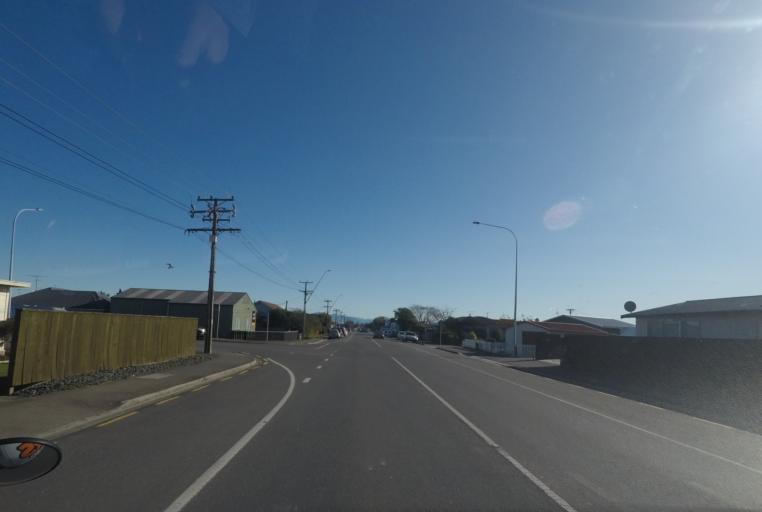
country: NZ
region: Nelson
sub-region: Nelson City
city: Nelson
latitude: -41.2919
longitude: 173.2451
